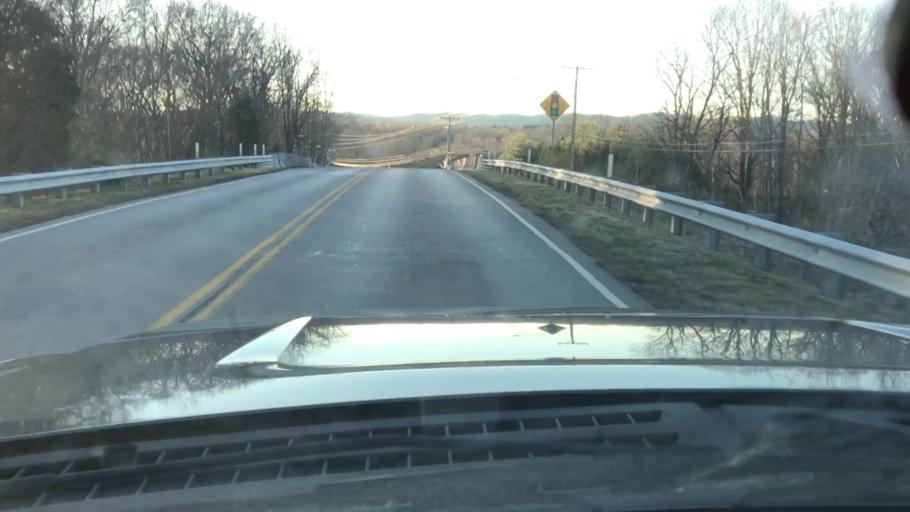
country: US
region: Tennessee
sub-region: Williamson County
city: Brentwood Estates
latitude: 35.9774
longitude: -86.7743
